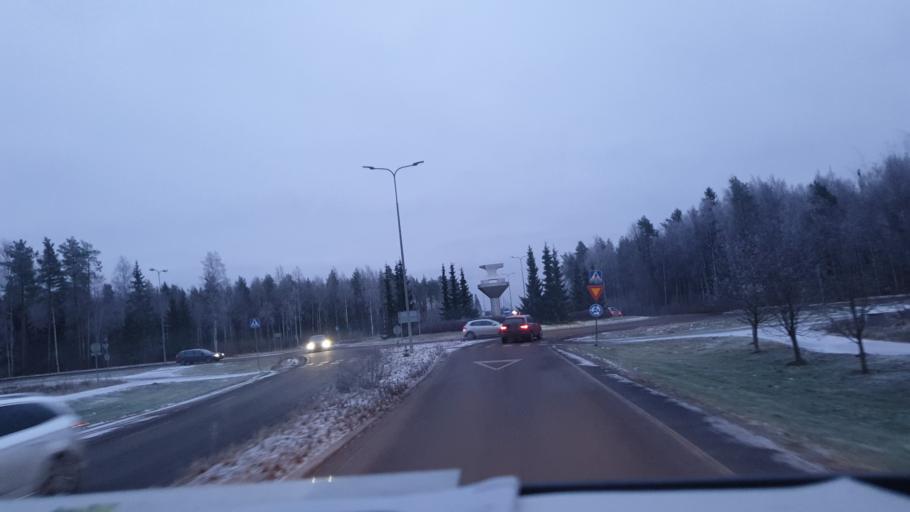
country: FI
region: Southern Ostrobothnia
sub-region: Seinaejoki
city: Nurmo
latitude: 62.7882
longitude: 22.9025
